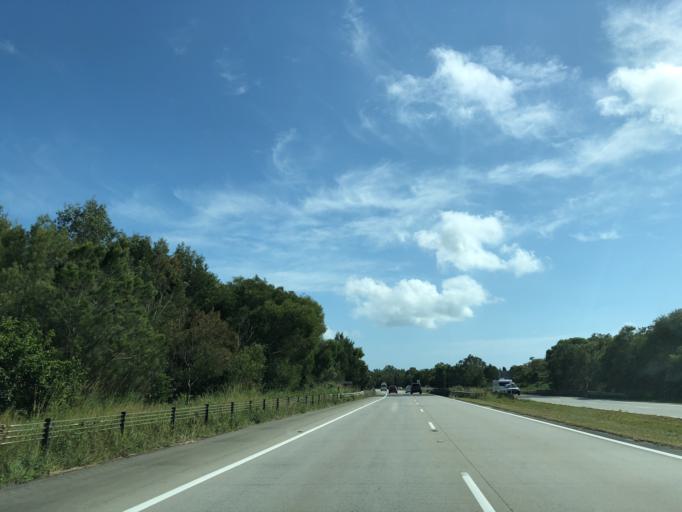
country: AU
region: New South Wales
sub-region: Byron Shire
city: Brunswick Heads
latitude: -28.5660
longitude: 153.5415
